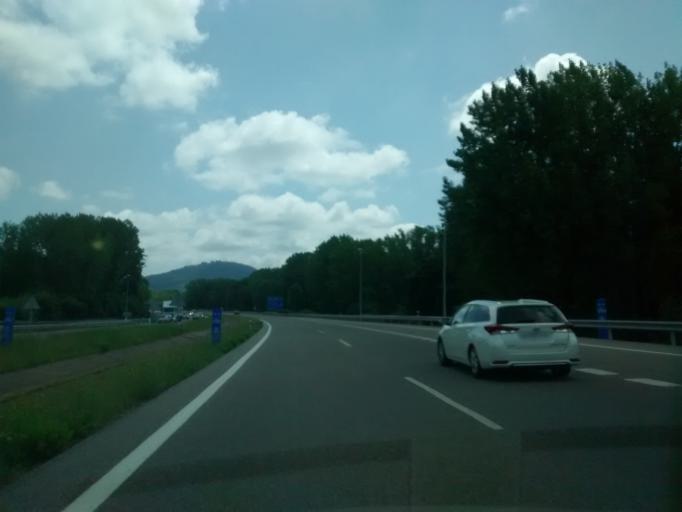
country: ES
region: Castille and Leon
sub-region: Provincia de Leon
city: Camponaraya
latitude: 42.5837
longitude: -6.6255
